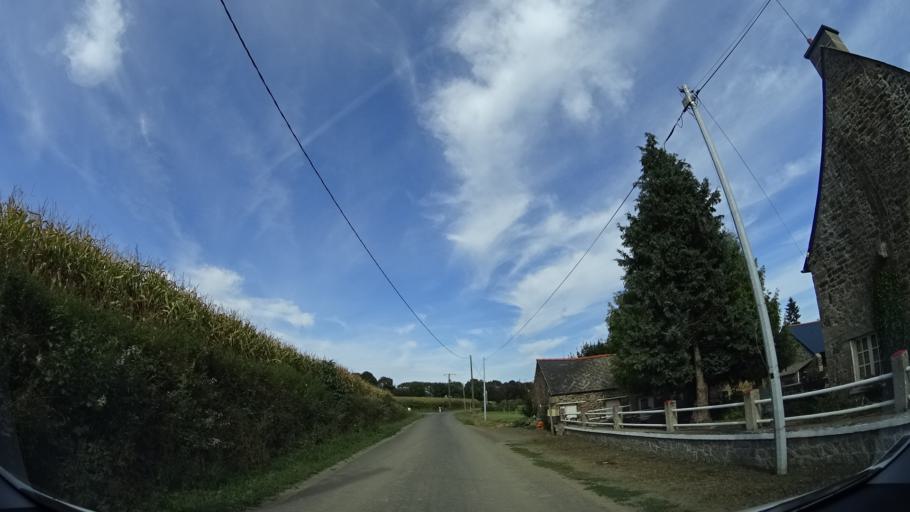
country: FR
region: Brittany
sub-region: Departement d'Ille-et-Vilaine
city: Romagne
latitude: 48.3197
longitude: -1.2771
